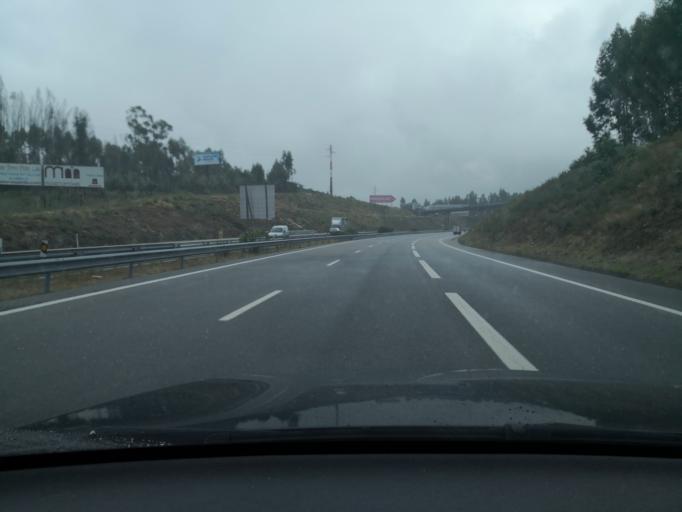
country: PT
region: Porto
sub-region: Pacos de Ferreira
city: Frazao
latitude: 41.2632
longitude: -8.3855
